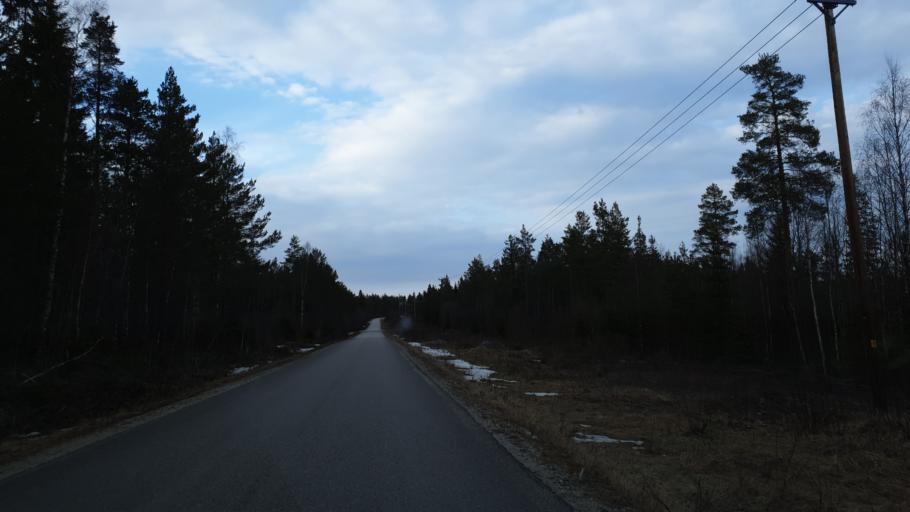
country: SE
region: Vaesternorrland
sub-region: Sundsvalls Kommun
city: Njurundabommen
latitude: 62.0015
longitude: 17.3901
